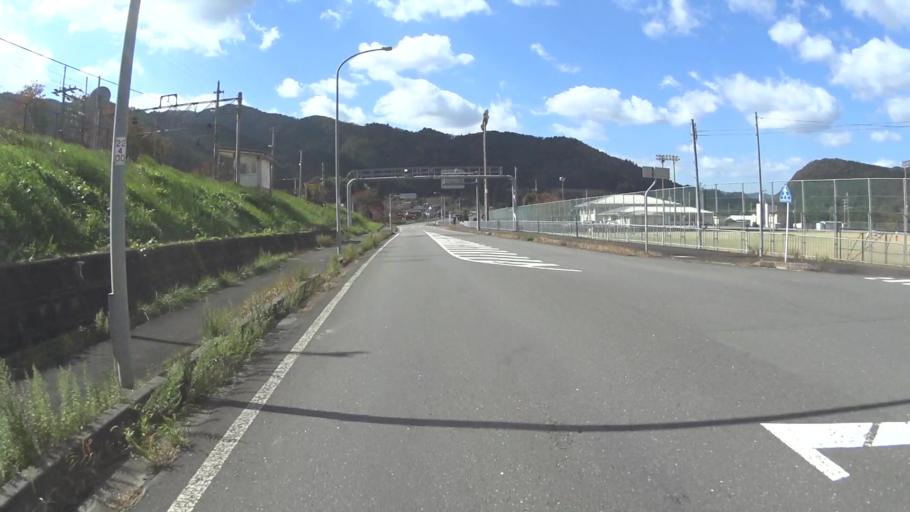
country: JP
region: Kyoto
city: Ayabe
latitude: 35.2663
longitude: 135.3858
